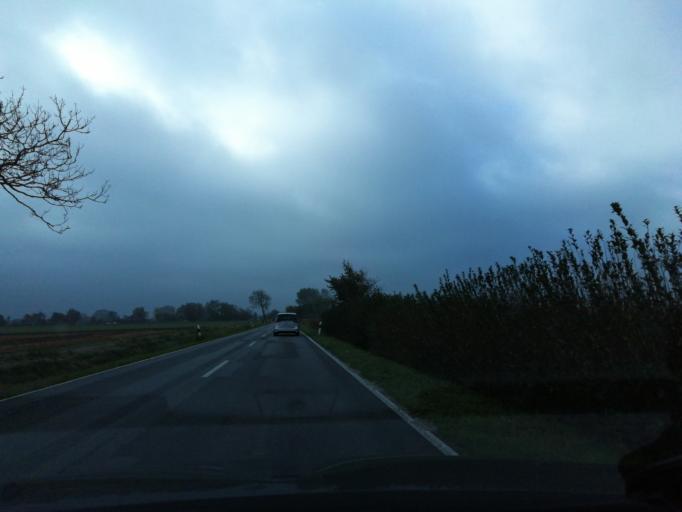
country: DE
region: Lower Saxony
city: Wangerooge
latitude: 53.6887
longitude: 7.8560
